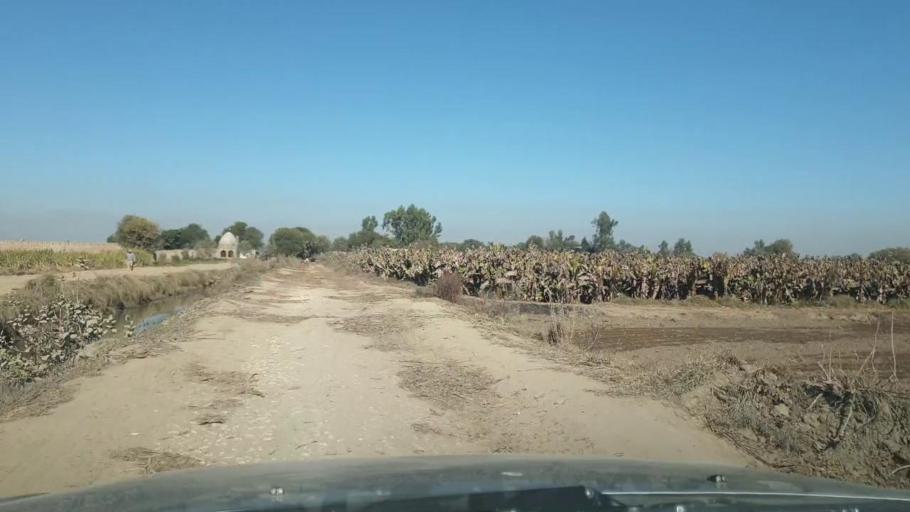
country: PK
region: Sindh
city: Ghotki
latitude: 28.0412
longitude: 69.2467
